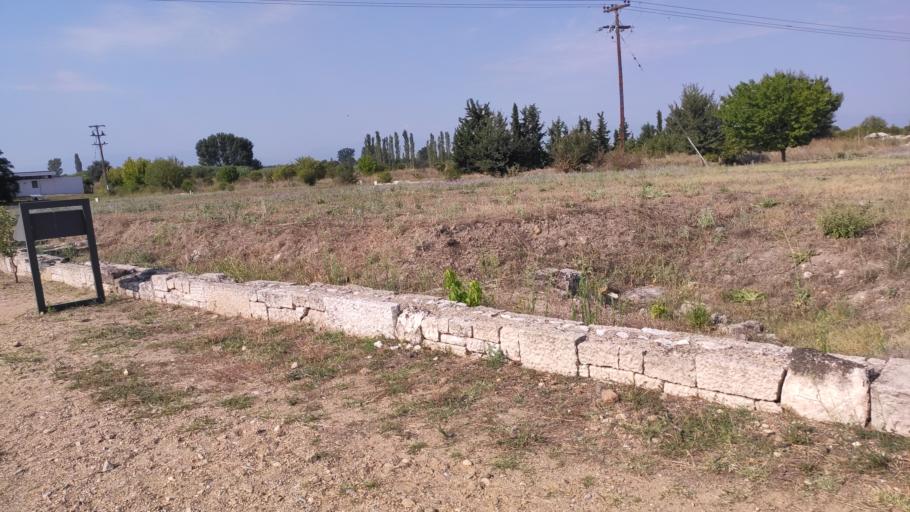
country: GR
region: Central Macedonia
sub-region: Nomos Pellis
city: Pella
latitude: 40.7529
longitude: 22.5179
